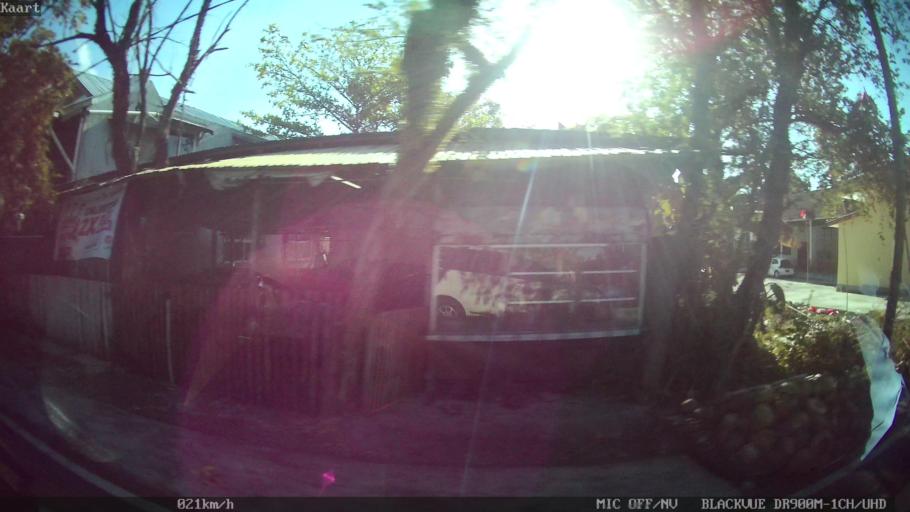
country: ID
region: Bali
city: Banjar Gunungpande
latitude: -8.6356
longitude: 115.1738
